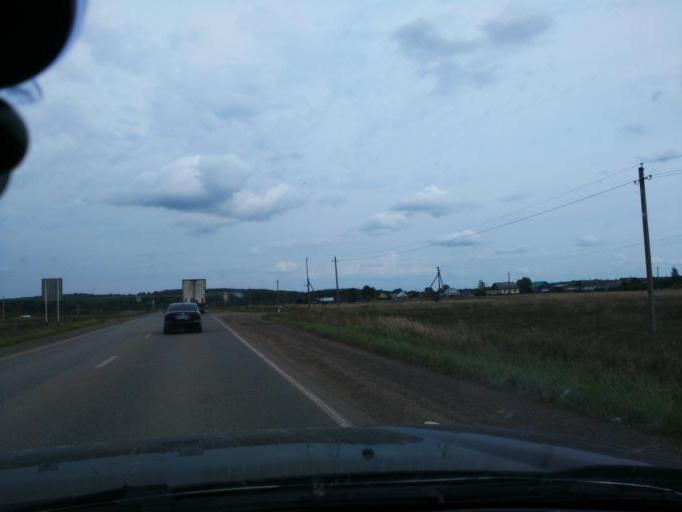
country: RU
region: Perm
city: Kuyeda
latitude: 56.4514
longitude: 55.6091
